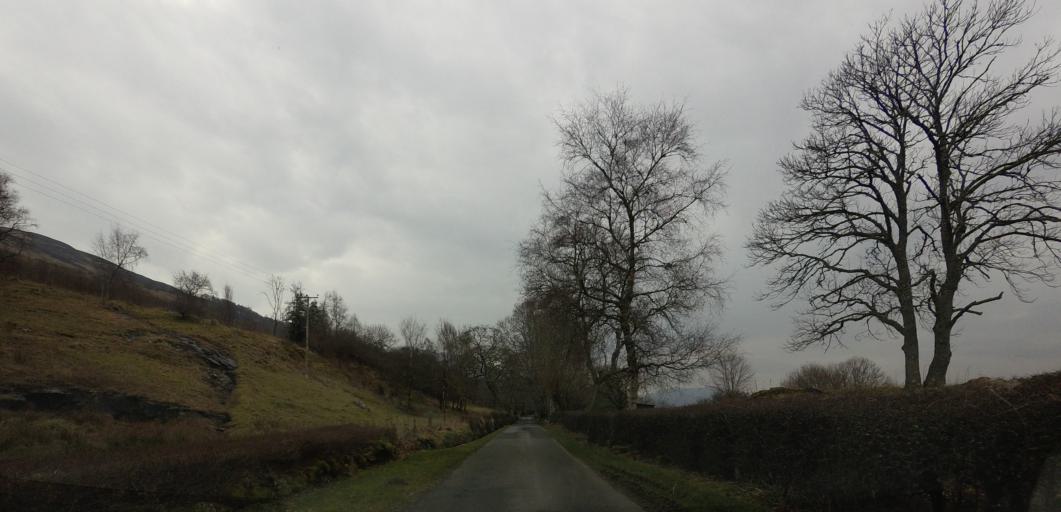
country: GB
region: Scotland
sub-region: Perth and Kinross
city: Comrie
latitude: 56.5398
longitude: -4.1027
